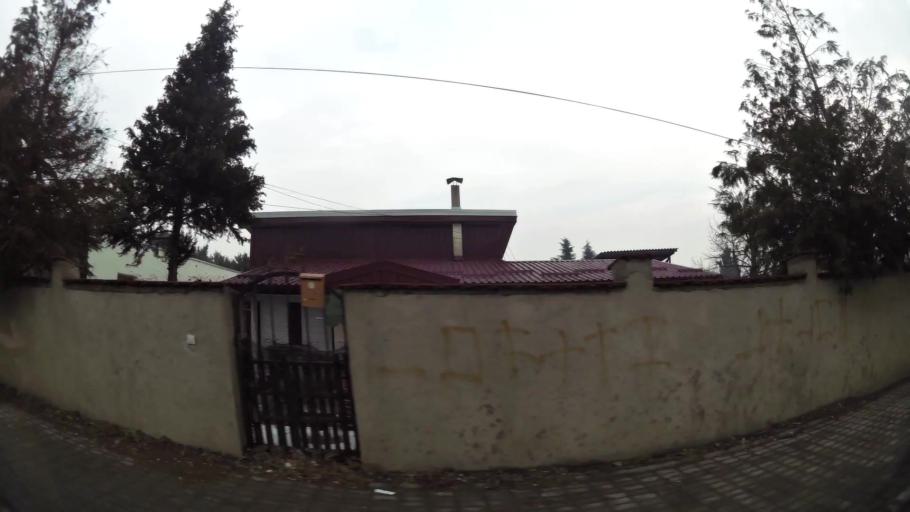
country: MK
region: Cair
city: Cair
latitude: 42.0139
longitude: 21.4572
